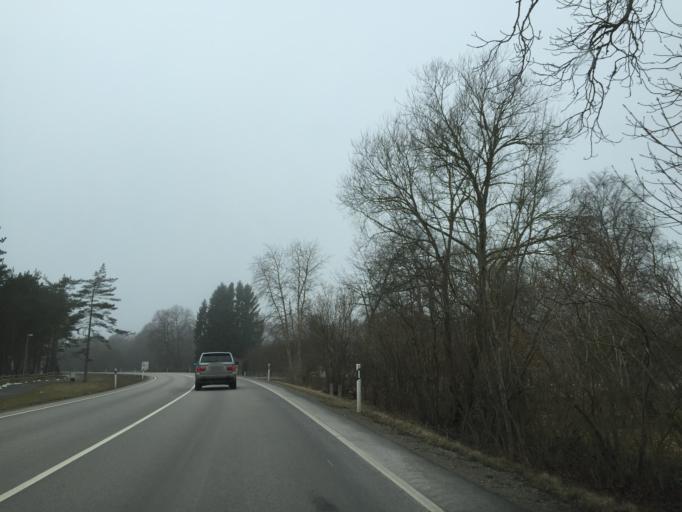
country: EE
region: Saare
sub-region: Kuressaare linn
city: Kuressaare
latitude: 58.2192
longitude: 22.3344
